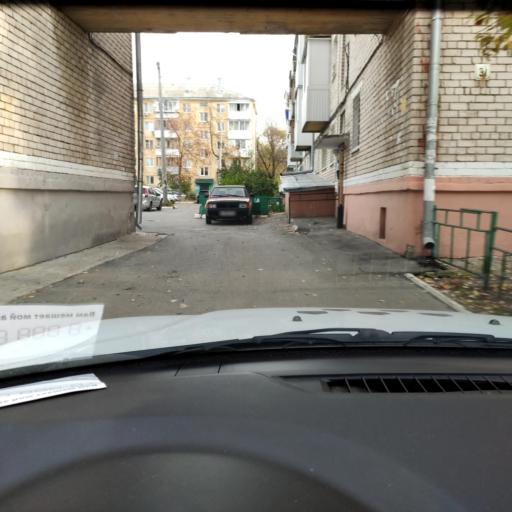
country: RU
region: Samara
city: Tol'yatti
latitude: 53.5104
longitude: 49.4030
